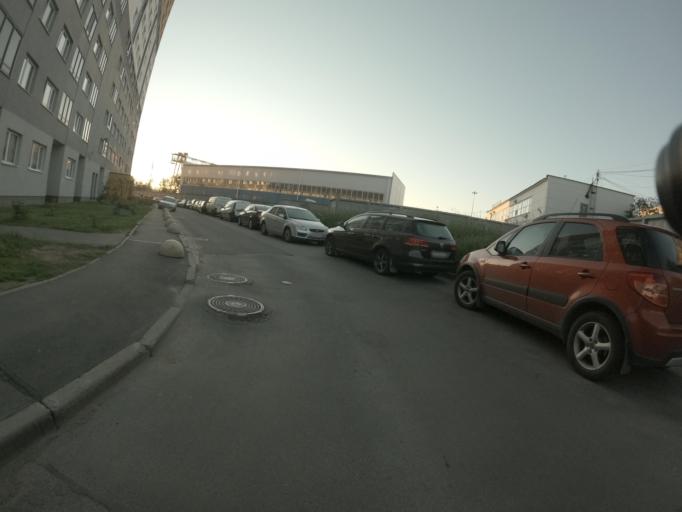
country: RU
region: St.-Petersburg
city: Krasnogvargeisky
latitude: 59.9790
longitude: 30.5146
